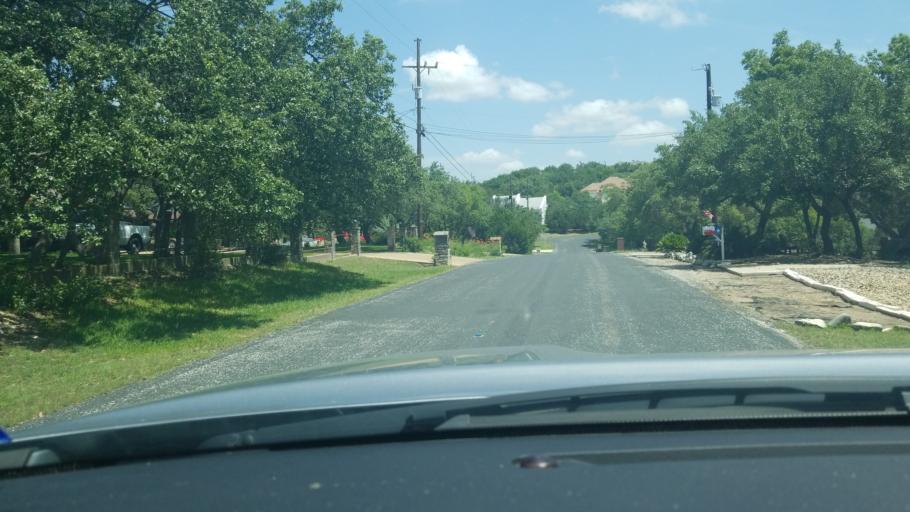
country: US
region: Texas
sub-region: Bexar County
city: Timberwood Park
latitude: 29.6899
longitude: -98.4839
